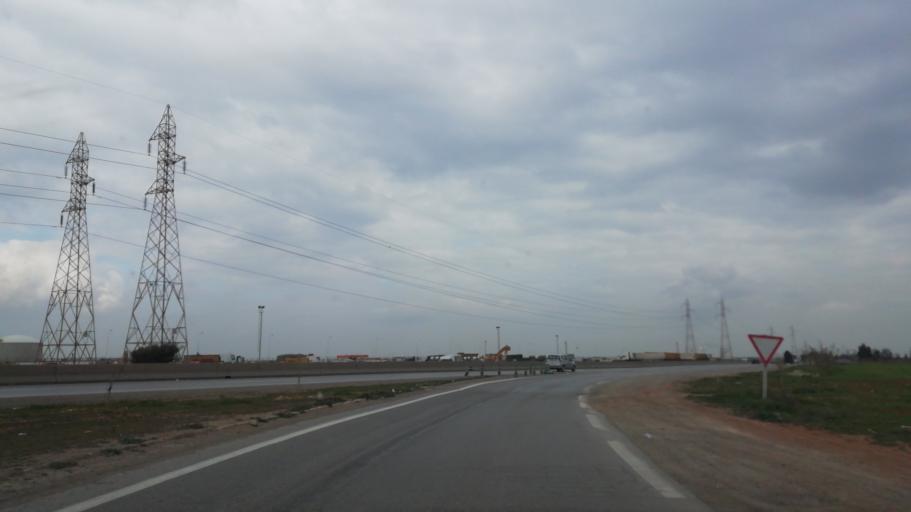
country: DZ
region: Oran
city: Ain el Bya
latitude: 35.7994
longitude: -0.3437
